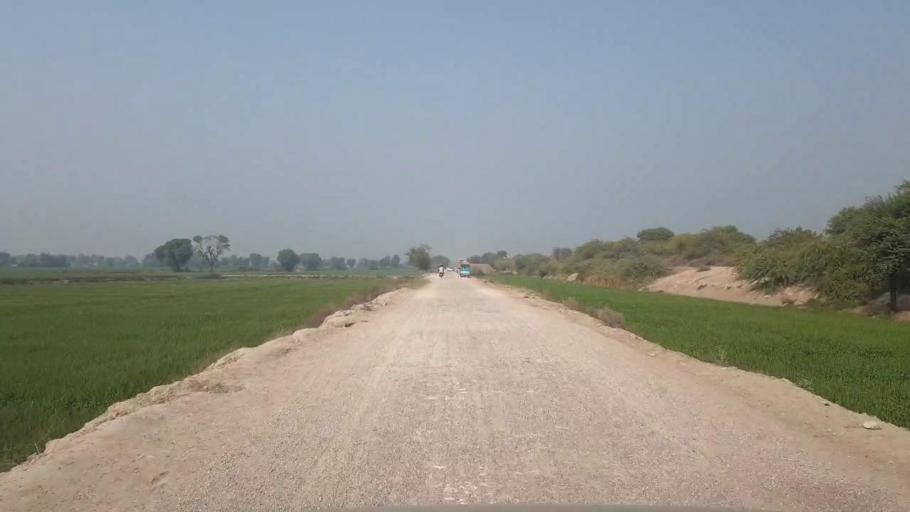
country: PK
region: Sindh
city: Hala
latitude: 25.8164
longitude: 68.4107
